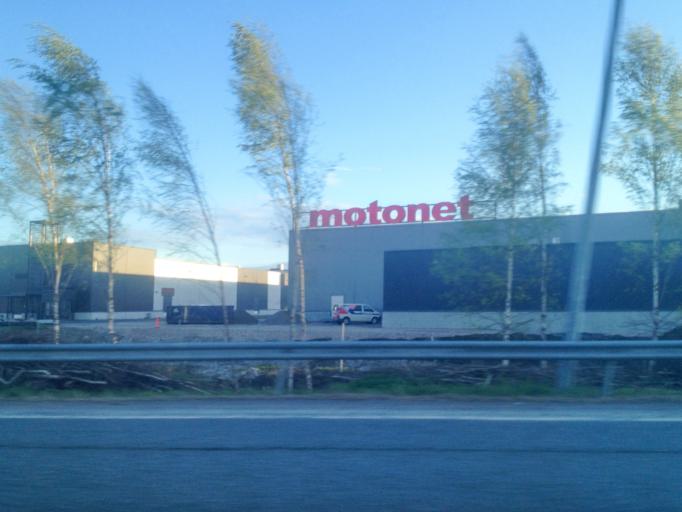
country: FI
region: Haeme
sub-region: Haemeenlinna
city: Haemeenlinna
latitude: 61.0139
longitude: 24.4142
